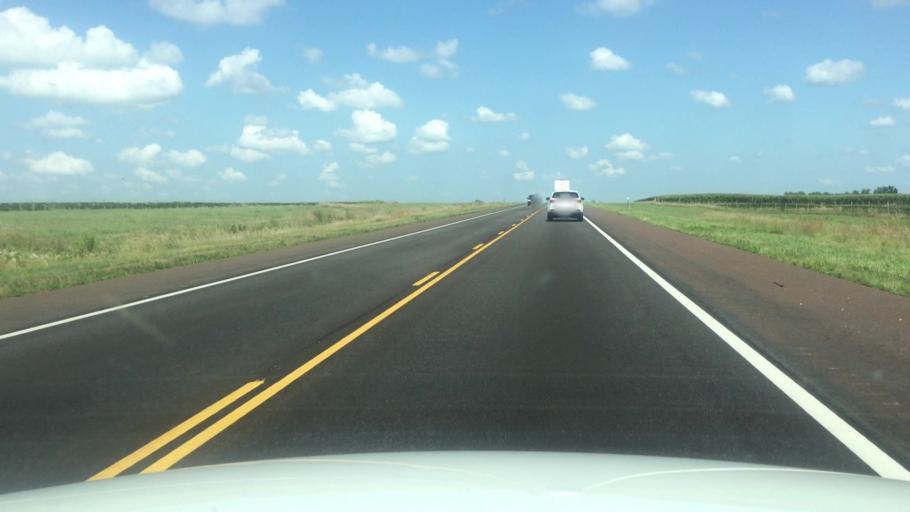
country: US
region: Kansas
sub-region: Nemaha County
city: Sabetha
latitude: 39.8620
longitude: -95.7650
